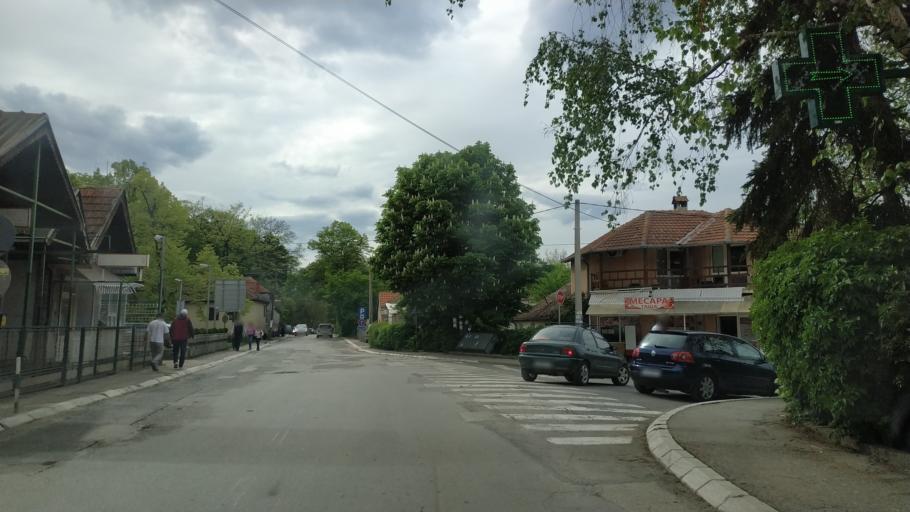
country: RS
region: Central Serbia
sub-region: Zajecarski Okrug
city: Soko Banja
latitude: 43.6453
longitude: 21.8755
